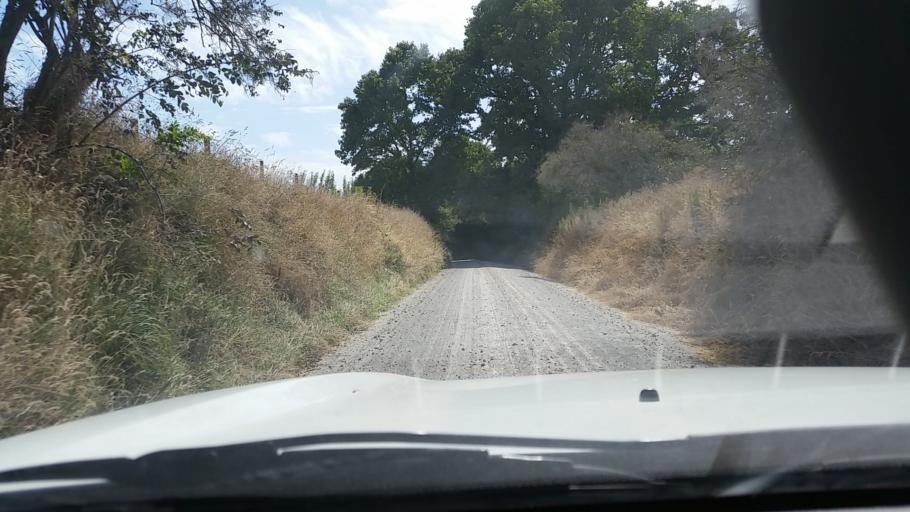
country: NZ
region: Bay of Plenty
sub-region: Rotorua District
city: Rotorua
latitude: -38.2437
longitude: 176.3430
